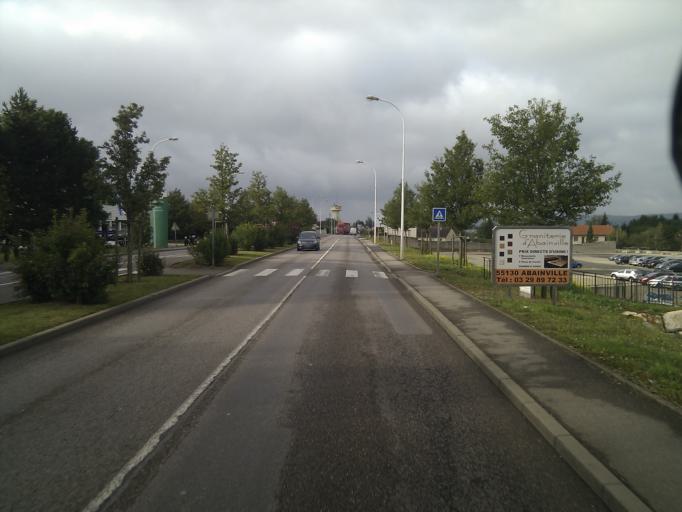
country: FR
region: Lorraine
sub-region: Departement des Vosges
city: Neufchateau
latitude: 48.3695
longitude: 5.7060
